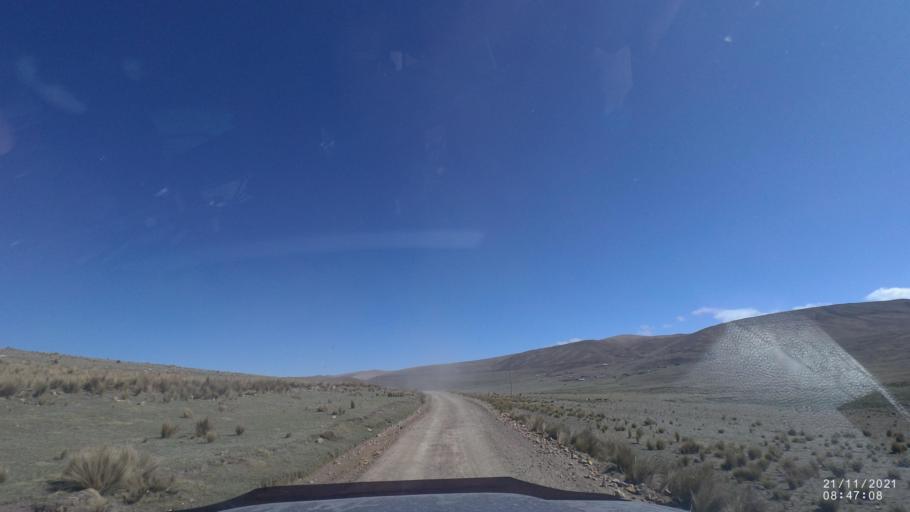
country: BO
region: Cochabamba
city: Cochabamba
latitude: -17.2383
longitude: -66.2332
